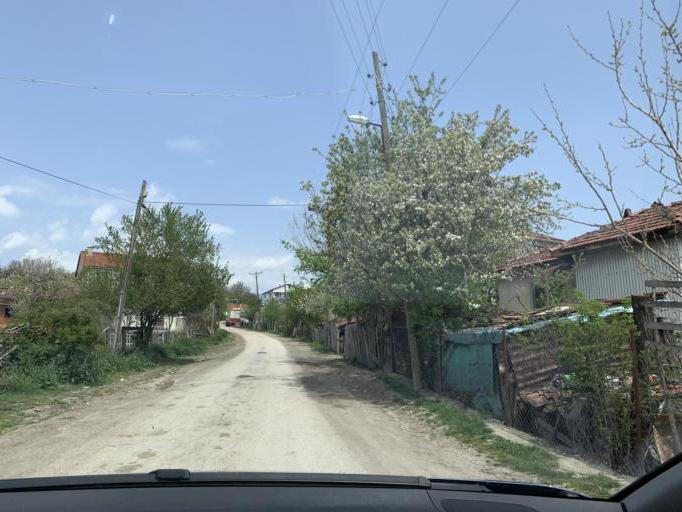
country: TR
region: Bolu
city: Bolu
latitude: 40.7632
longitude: 31.7075
